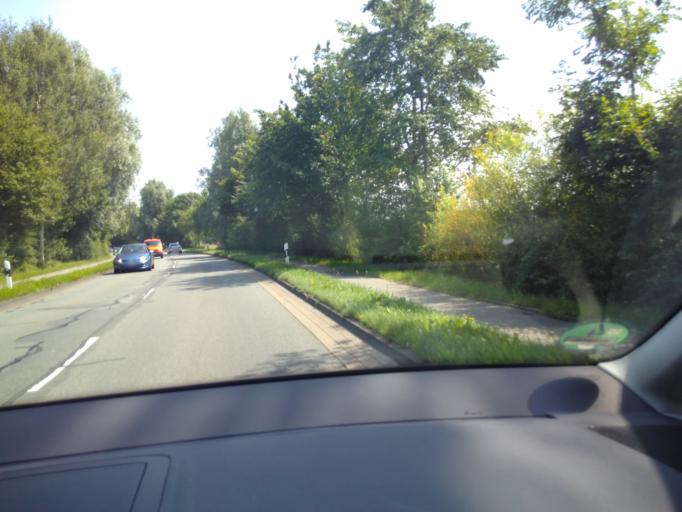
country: DE
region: Lower Saxony
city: Cuxhaven
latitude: 53.8453
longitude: 8.6774
